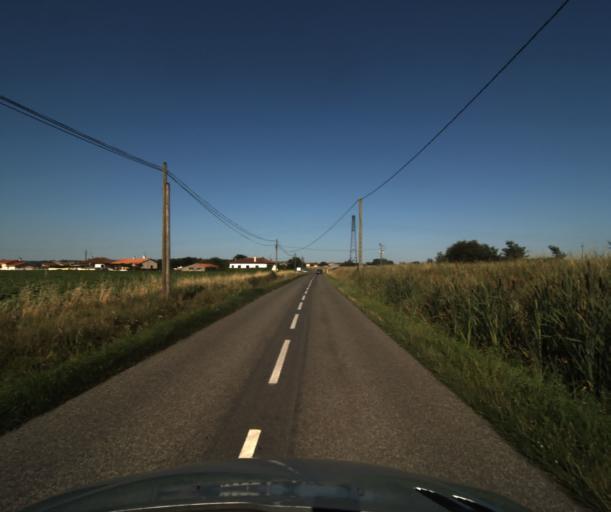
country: FR
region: Midi-Pyrenees
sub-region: Departement de la Haute-Garonne
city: Saubens
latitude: 43.4767
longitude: 1.3702
